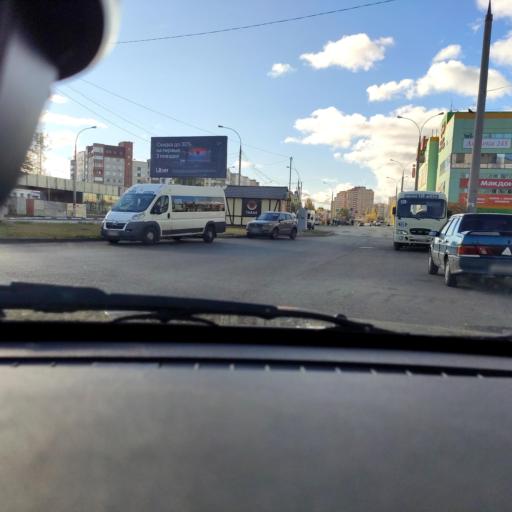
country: RU
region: Samara
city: Tol'yatti
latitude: 53.5454
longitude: 49.3610
